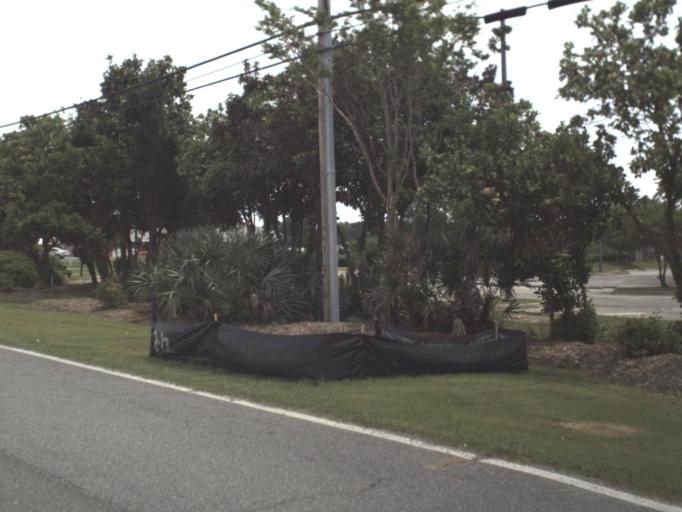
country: US
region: Florida
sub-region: Santa Rosa County
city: Tiger Point
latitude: 30.3927
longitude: -87.0471
